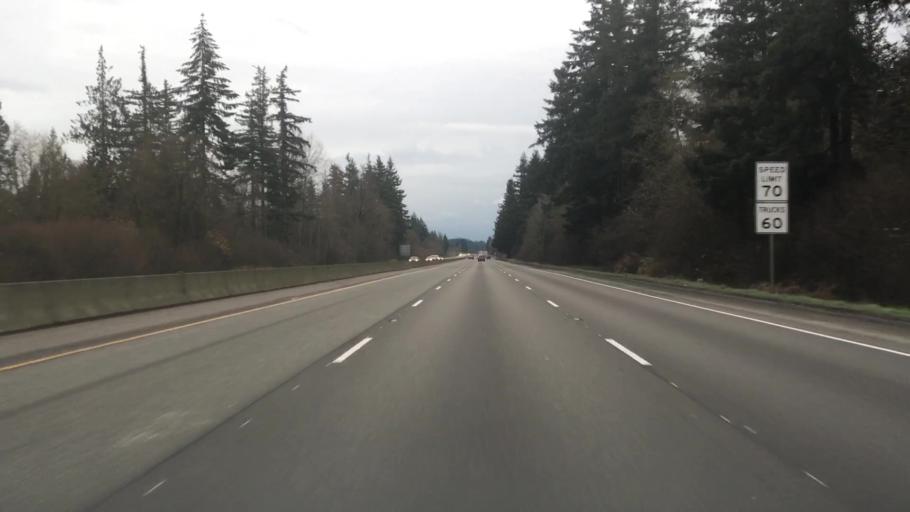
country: US
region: Washington
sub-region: Thurston County
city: Tumwater
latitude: 46.9433
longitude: -122.9404
